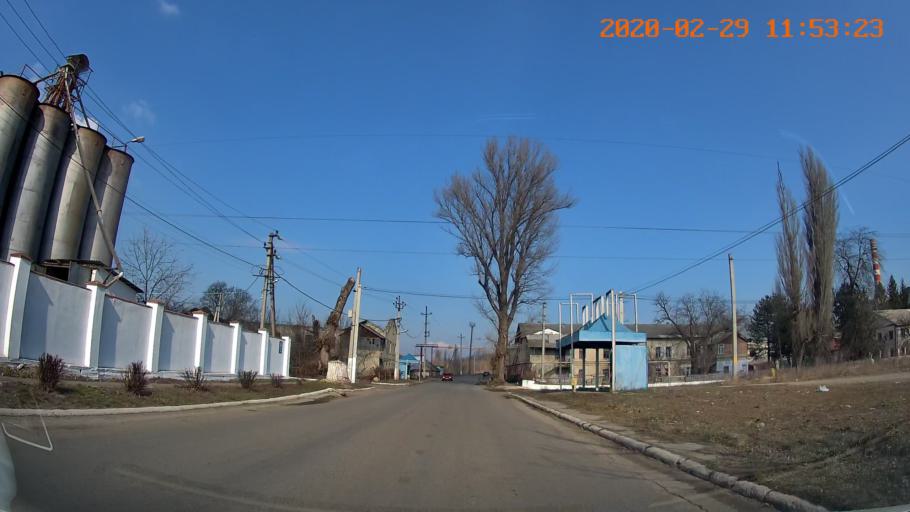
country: MD
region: Telenesti
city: Ribnita
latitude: 47.7771
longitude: 28.9908
